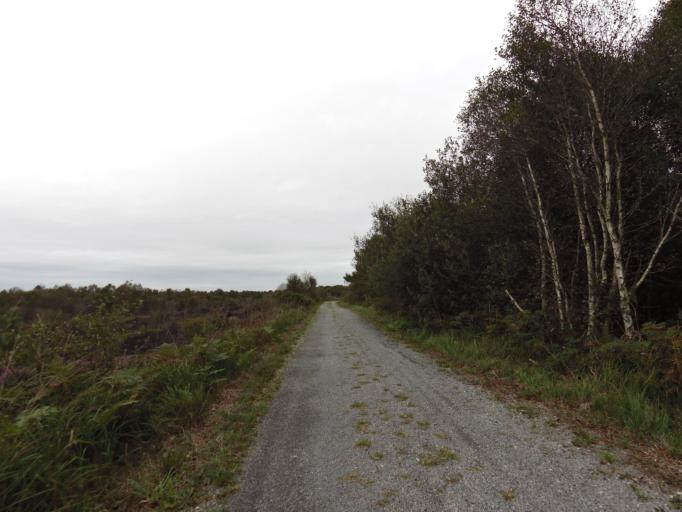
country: IE
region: Leinster
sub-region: Uibh Fhaili
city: Ferbane
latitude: 53.2408
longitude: -7.7573
